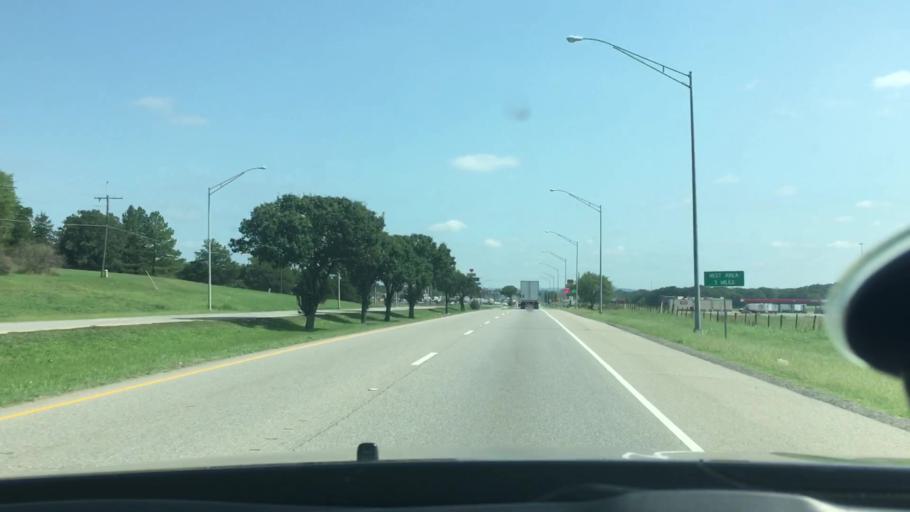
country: US
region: Oklahoma
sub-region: Atoka County
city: Atoka
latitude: 34.3614
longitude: -96.1437
